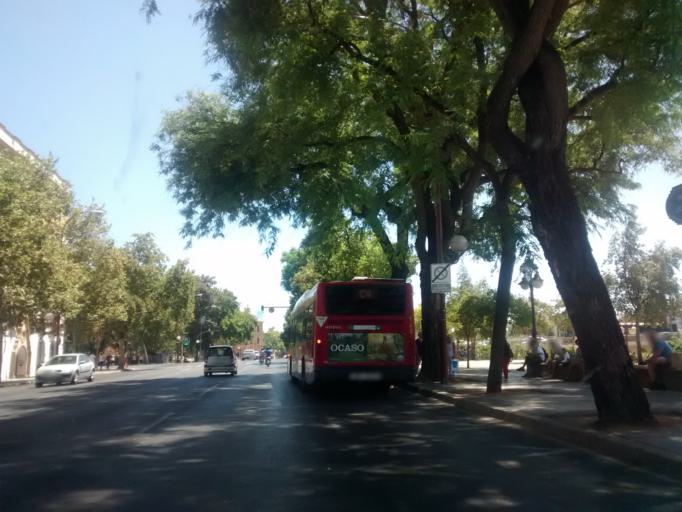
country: ES
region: Andalusia
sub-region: Provincia de Sevilla
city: Sevilla
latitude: 37.3822
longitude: -5.9959
